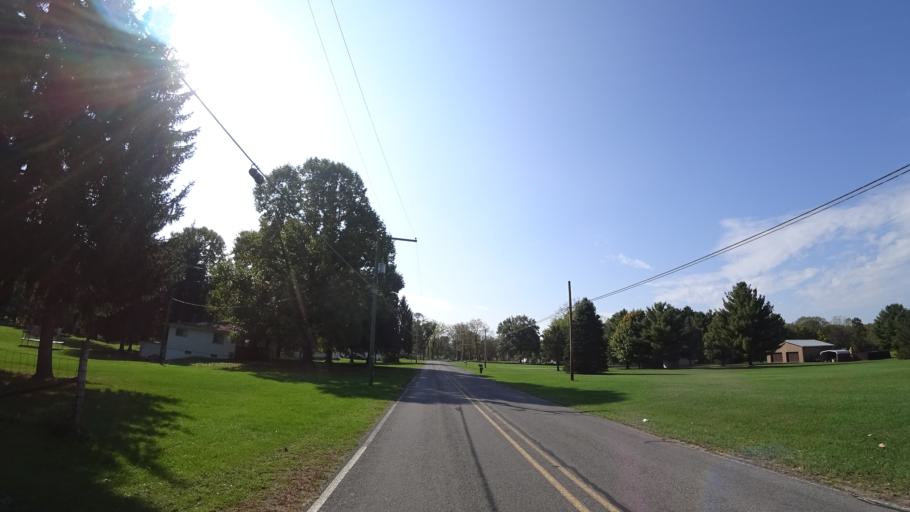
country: US
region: Michigan
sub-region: Saint Joseph County
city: Three Rivers
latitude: 41.9233
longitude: -85.6358
